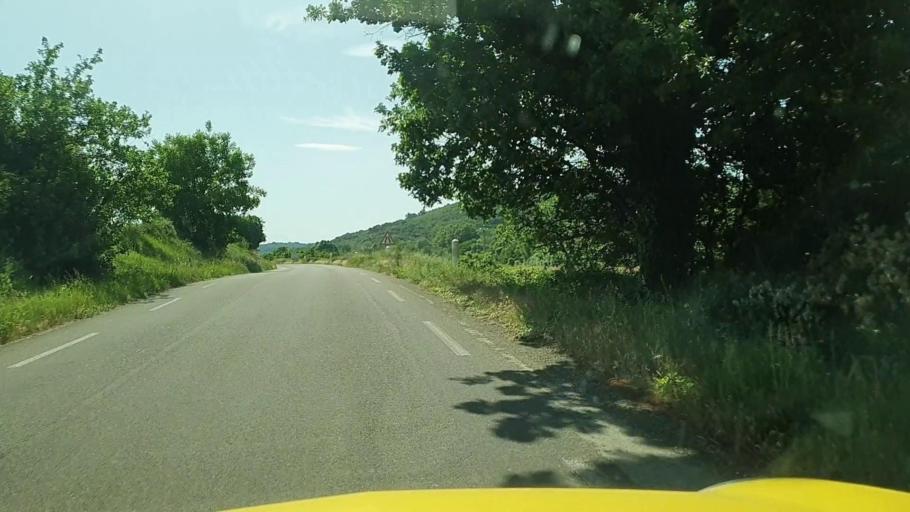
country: FR
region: Languedoc-Roussillon
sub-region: Departement du Gard
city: Tresques
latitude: 44.0982
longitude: 4.5487
